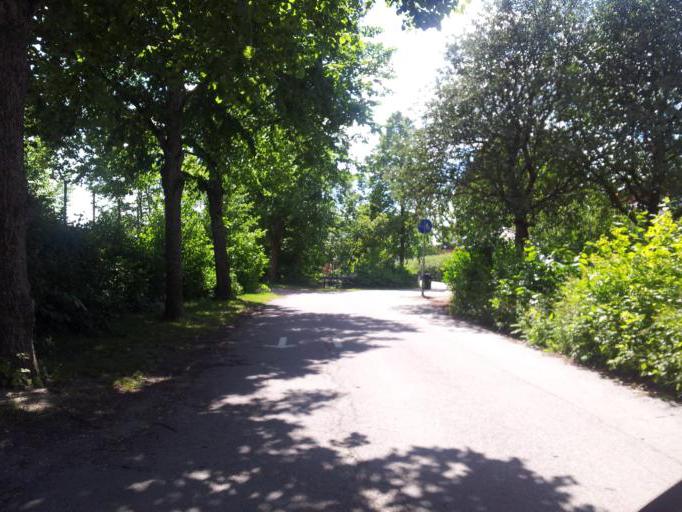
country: SE
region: Uppsala
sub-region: Uppsala Kommun
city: Uppsala
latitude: 59.8689
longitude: 17.6515
